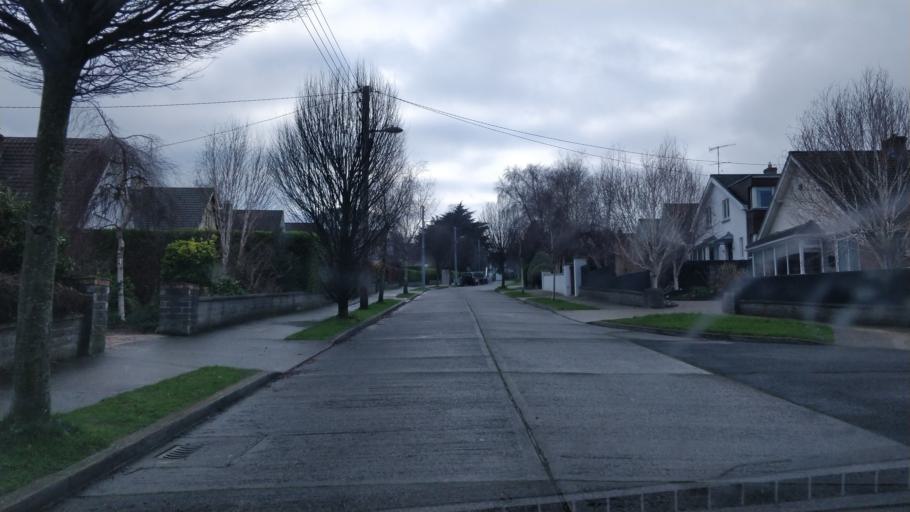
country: IE
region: Leinster
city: Foxrock
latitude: 53.2772
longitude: -6.1764
